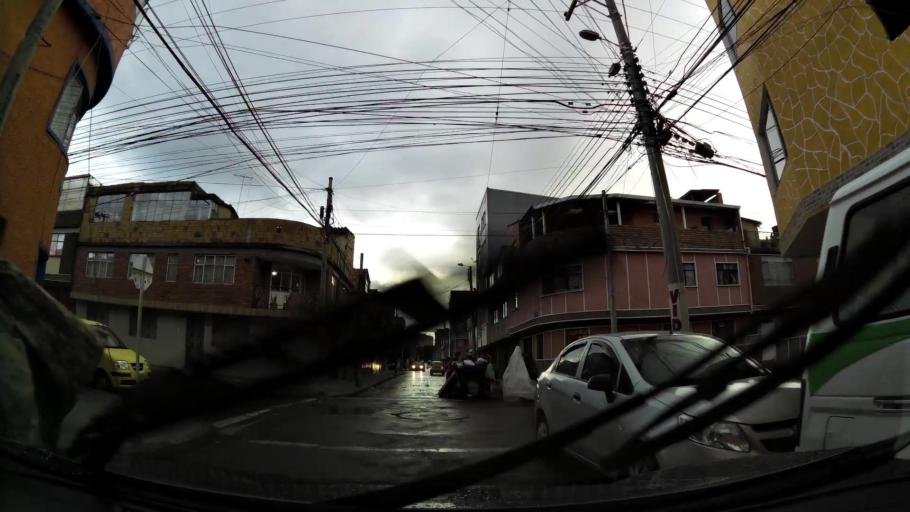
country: CO
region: Bogota D.C.
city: Barrio San Luis
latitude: 4.6785
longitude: -74.0785
